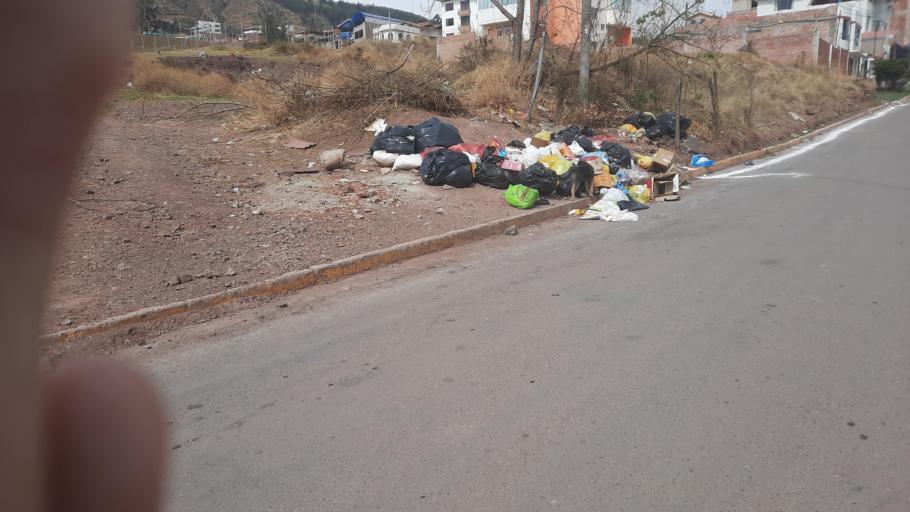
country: PE
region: Cusco
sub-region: Provincia de Cusco
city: Saylla
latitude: -13.5276
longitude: -71.9008
